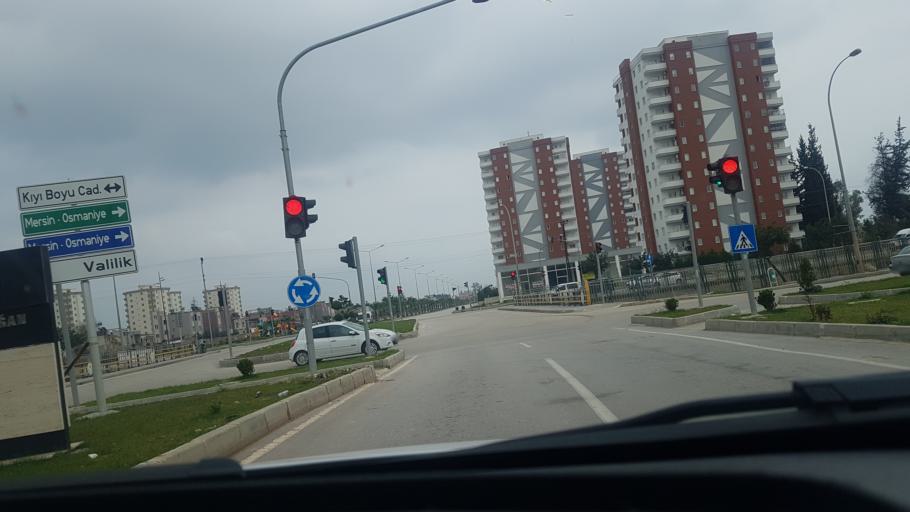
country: TR
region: Adana
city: Seyhan
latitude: 37.0078
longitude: 35.2574
